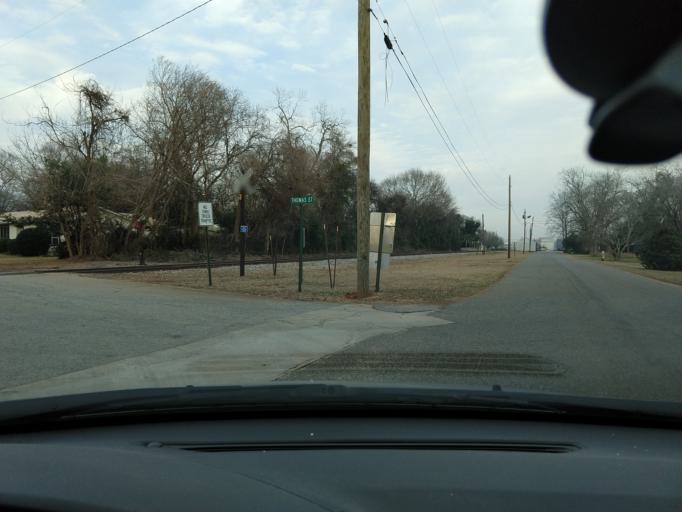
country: US
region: Georgia
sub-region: Webster County
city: Preston
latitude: 32.0325
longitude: -84.3976
